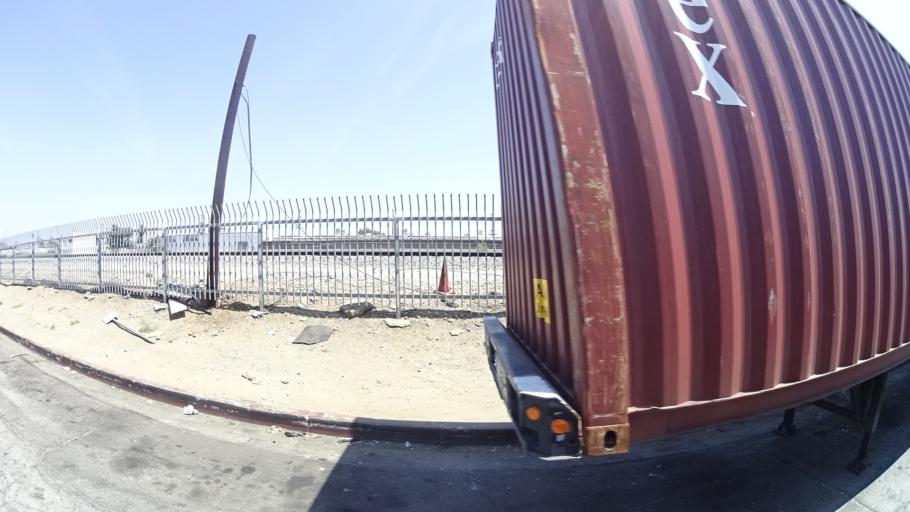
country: US
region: California
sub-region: Los Angeles County
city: Van Nuys
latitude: 34.2123
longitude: -118.4528
